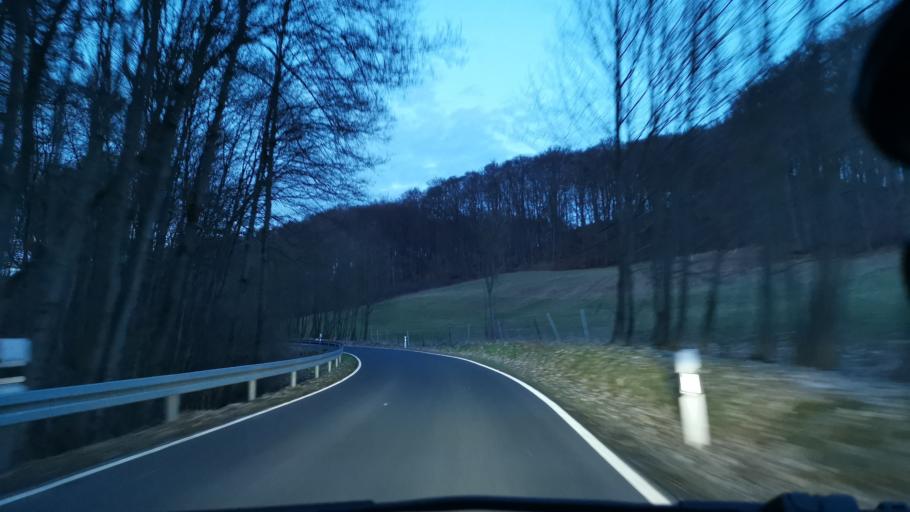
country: DE
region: Hesse
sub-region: Regierungsbezirk Kassel
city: Cornberg
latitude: 51.0747
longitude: 9.8191
